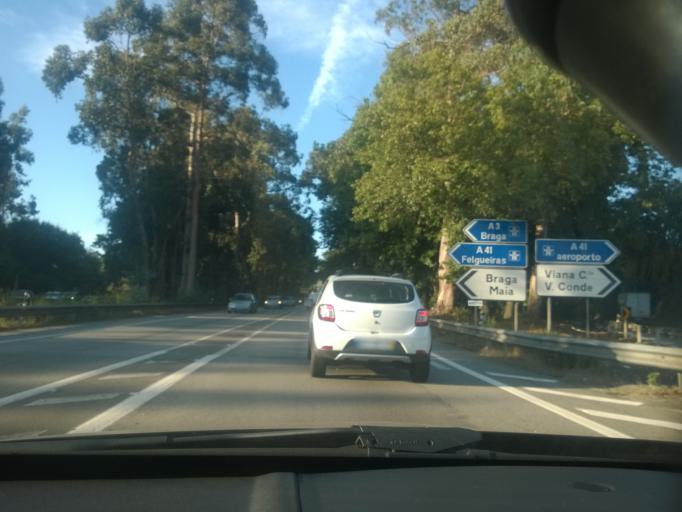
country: PT
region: Porto
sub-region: Maia
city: Leca do Bailio
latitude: 41.2210
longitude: -8.6268
